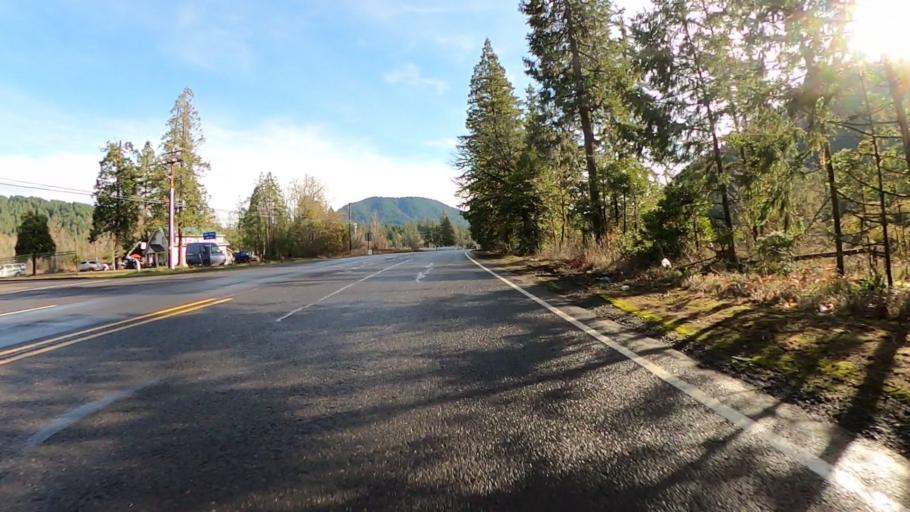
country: US
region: Oregon
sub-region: Lane County
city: Oakridge
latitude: 43.7363
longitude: -122.4496
